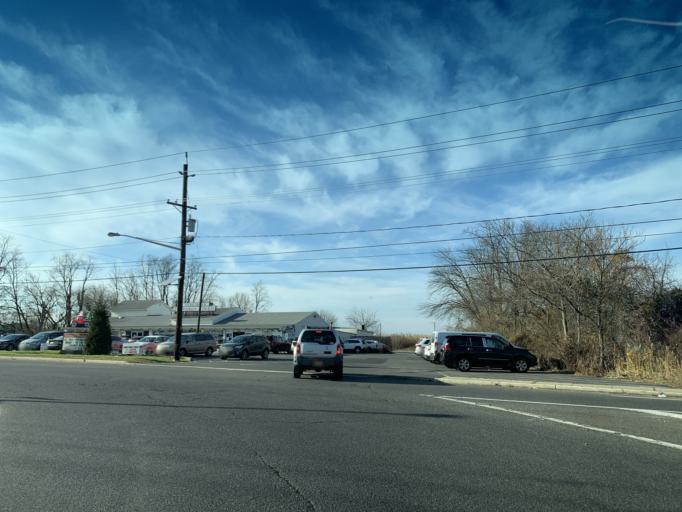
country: US
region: New Jersey
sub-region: Camden County
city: Brooklawn
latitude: 39.8770
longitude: -75.1245
